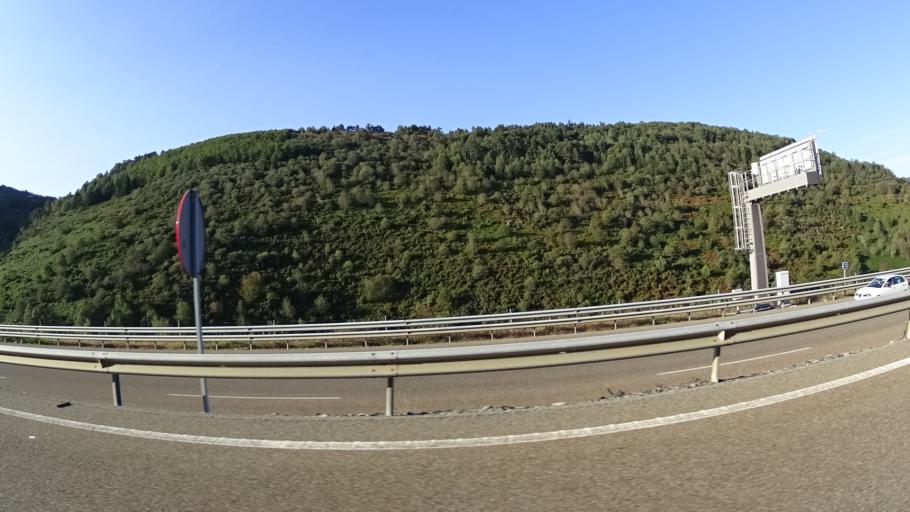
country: ES
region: Castille and Leon
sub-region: Provincia de Leon
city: Balboa
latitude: 42.7294
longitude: -7.0401
